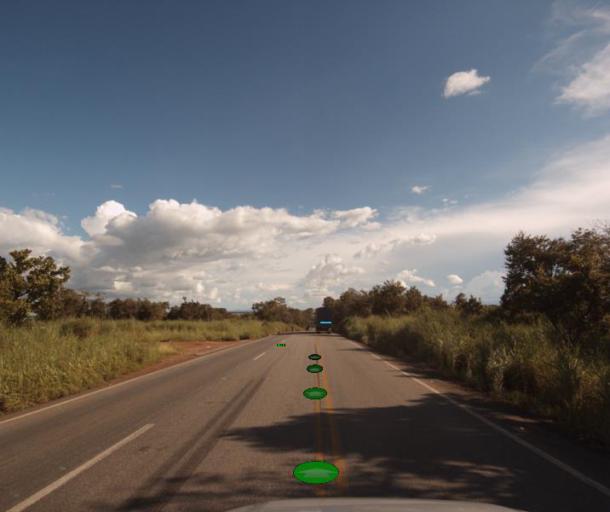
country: BR
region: Goias
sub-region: Porangatu
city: Porangatu
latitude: -13.0872
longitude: -49.1925
